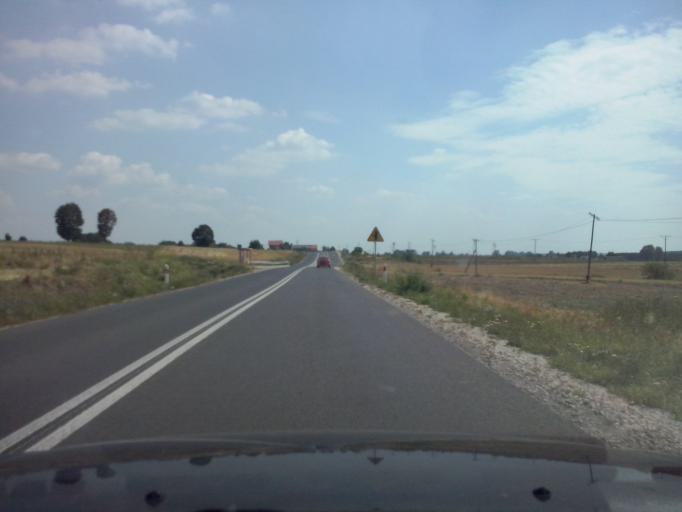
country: PL
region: Swietokrzyskie
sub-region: Powiat buski
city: Gnojno
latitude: 50.5882
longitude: 20.9026
